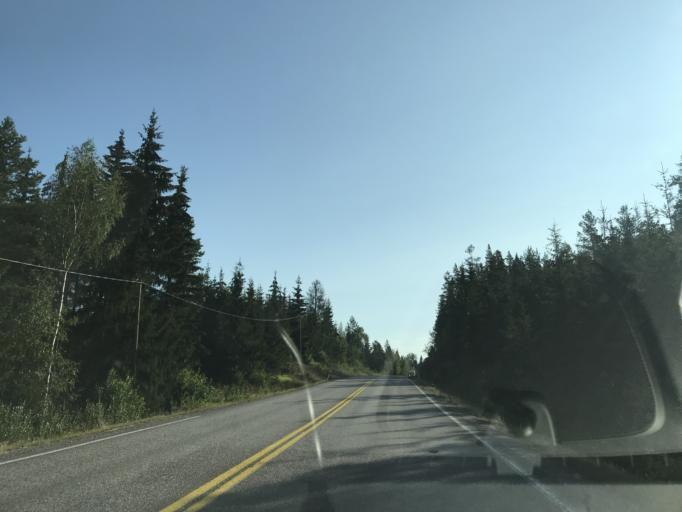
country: FI
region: Uusimaa
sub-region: Porvoo
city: Pukkila
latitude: 60.7798
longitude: 25.5783
